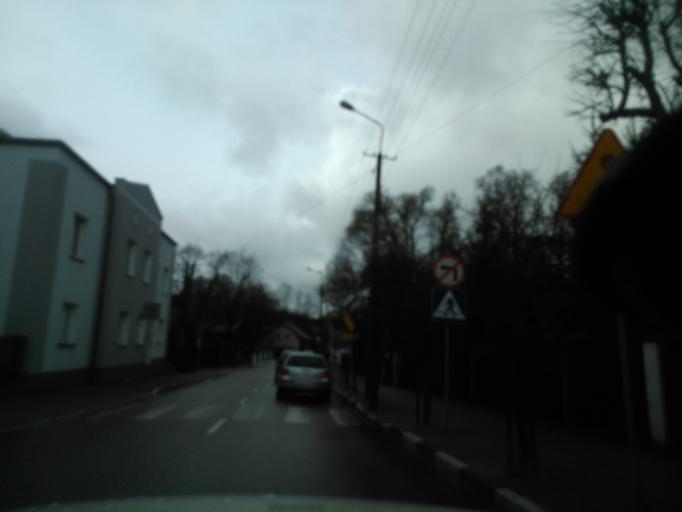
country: PL
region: Warmian-Masurian Voivodeship
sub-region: Powiat dzialdowski
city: Lidzbark
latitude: 53.2665
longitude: 19.8198
